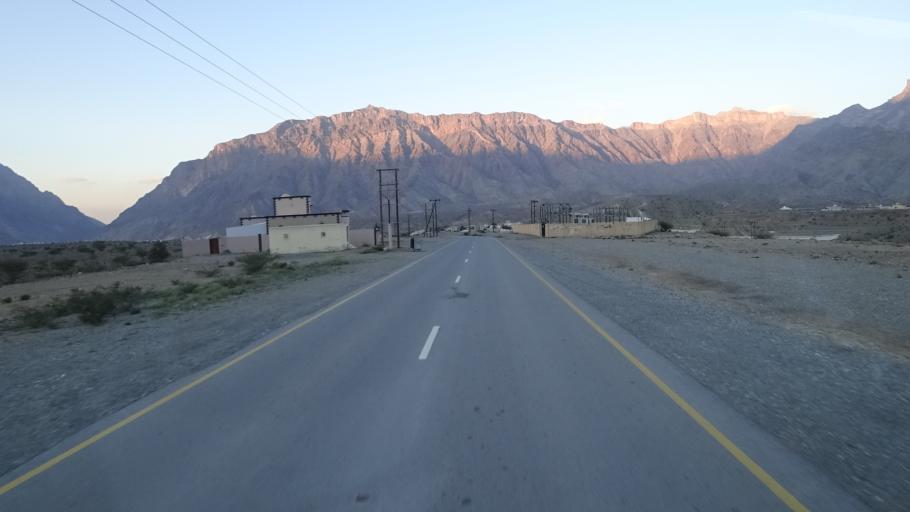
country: OM
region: Al Batinah
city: Rustaq
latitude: 23.2809
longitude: 57.3286
